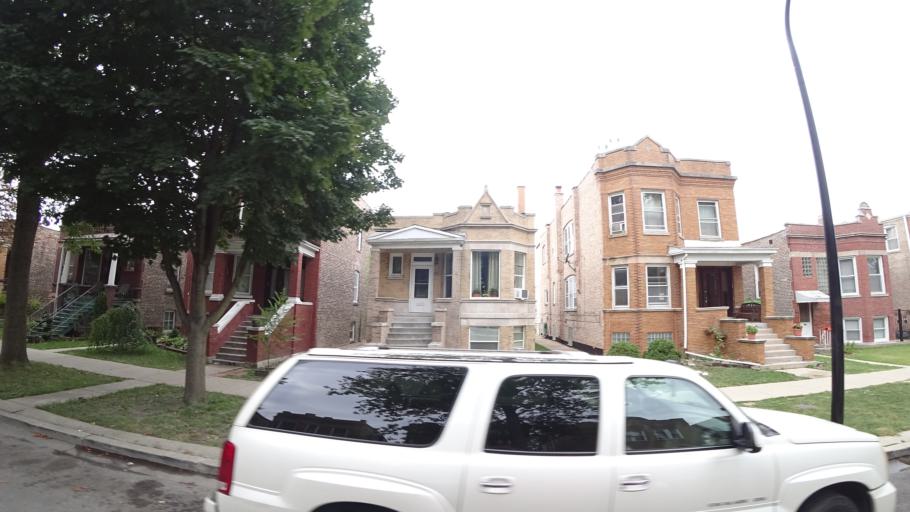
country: US
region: Illinois
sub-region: Cook County
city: Cicero
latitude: 41.8522
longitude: -87.7652
